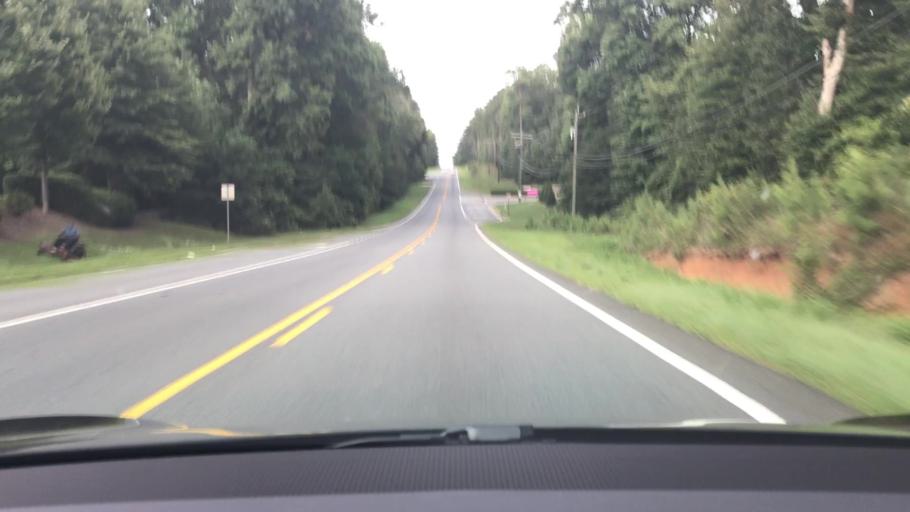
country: US
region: Georgia
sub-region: Gwinnett County
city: Suwanee
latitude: 34.0255
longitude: -84.1044
